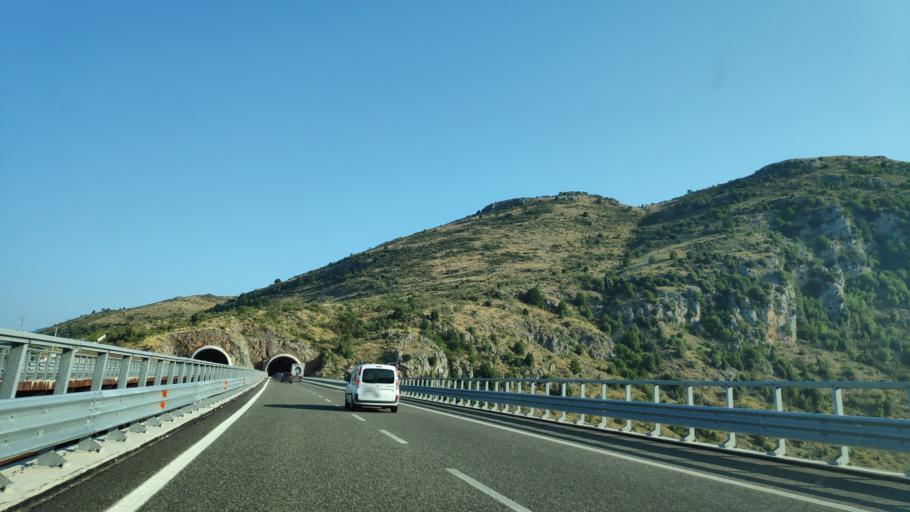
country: IT
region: Basilicate
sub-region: Provincia di Potenza
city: Lauria
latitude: 40.0355
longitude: 15.8739
